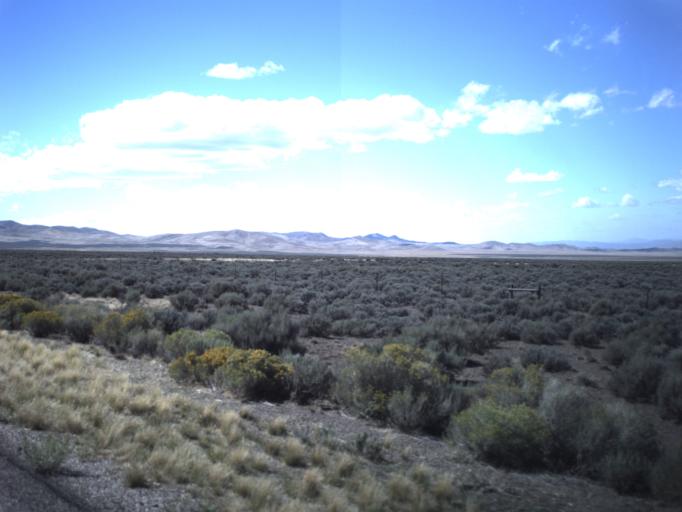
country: US
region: Utah
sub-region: Beaver County
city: Milford
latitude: 38.1891
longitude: -112.9383
